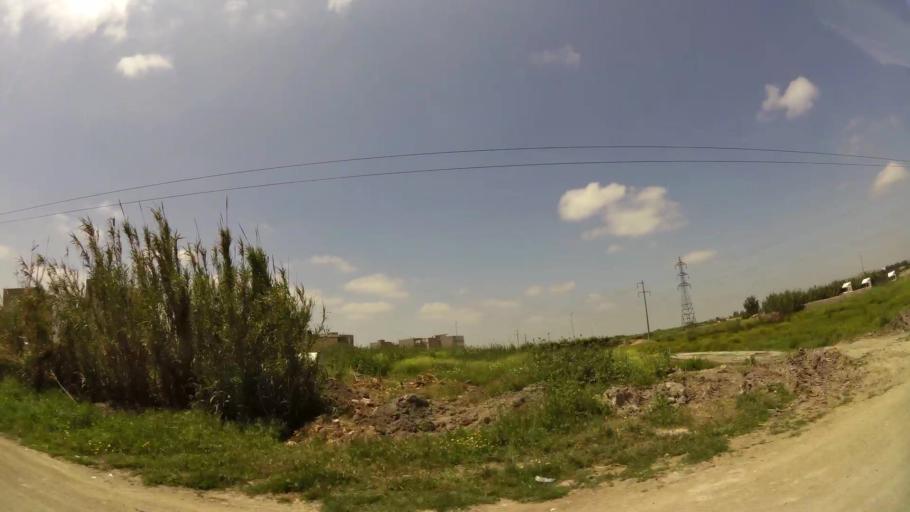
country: MA
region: Fes-Boulemane
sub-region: Fes
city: Fes
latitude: 34.0359
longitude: -5.0605
